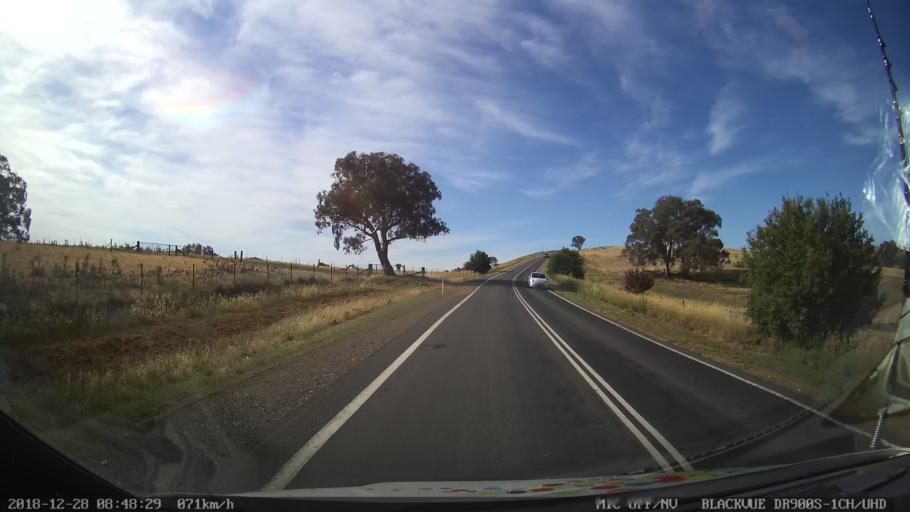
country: AU
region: New South Wales
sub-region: Upper Lachlan Shire
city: Crookwell
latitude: -34.0374
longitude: 149.3367
